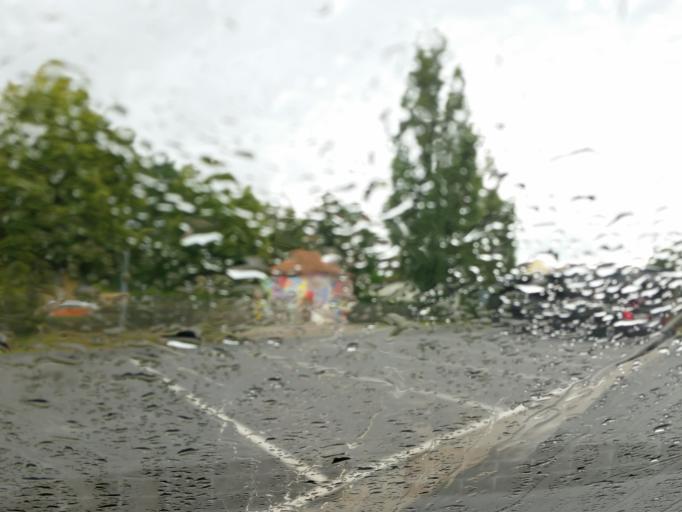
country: DE
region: Saxony
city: Bautzen
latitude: 51.1858
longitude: 14.4243
